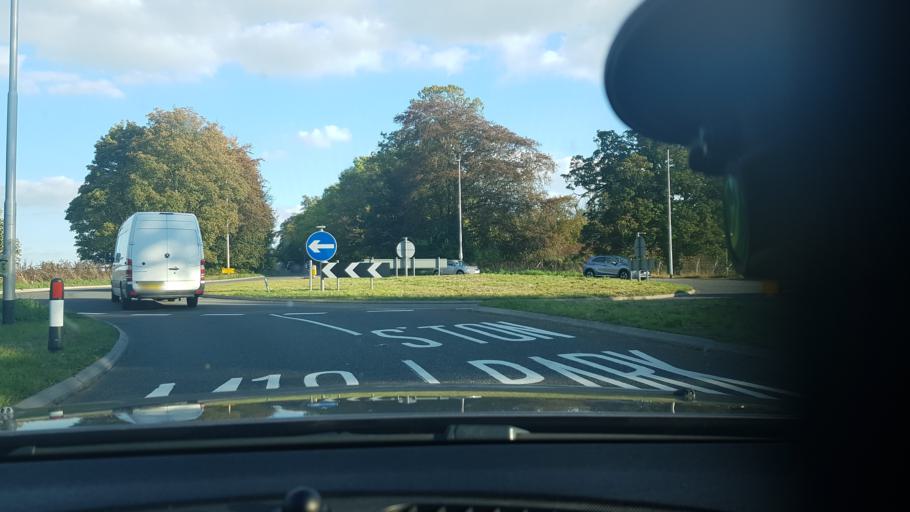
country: GB
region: England
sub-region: Gloucestershire
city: Cirencester
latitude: 51.7029
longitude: -1.9433
